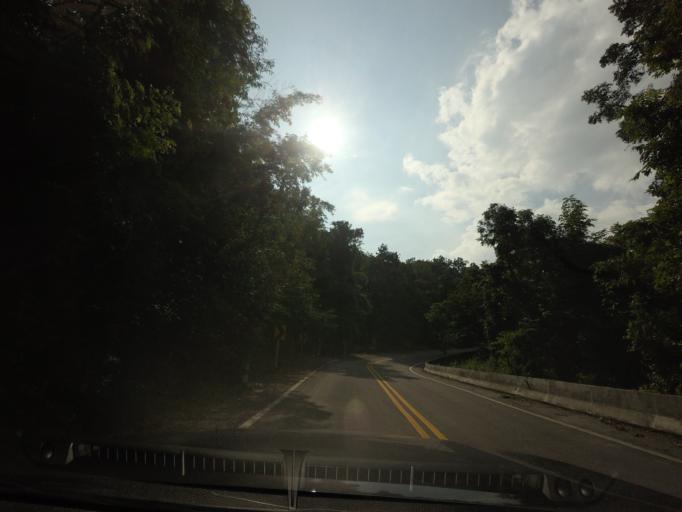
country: TH
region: Nan
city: Na Noi
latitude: 18.2781
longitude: 100.9701
